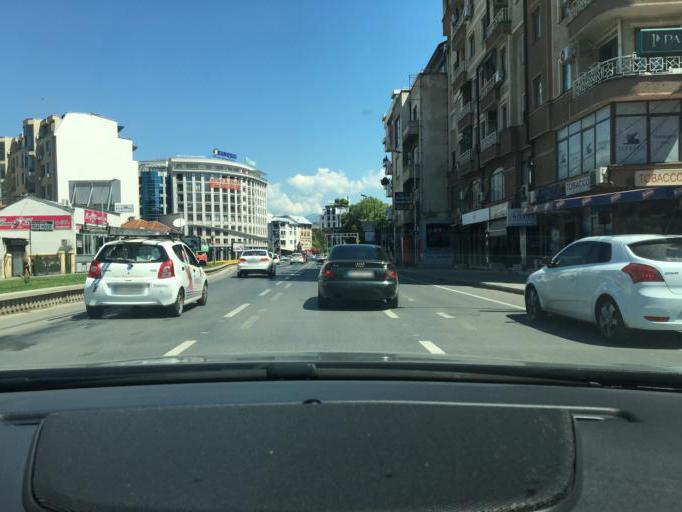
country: MK
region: Karpos
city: Skopje
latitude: 41.9970
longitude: 21.4251
